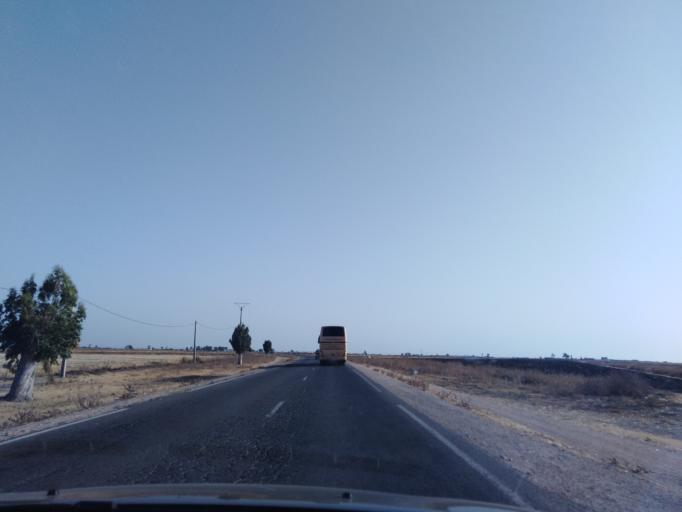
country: MA
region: Doukkala-Abda
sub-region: Safi
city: Youssoufia
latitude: 32.4859
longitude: -8.7672
